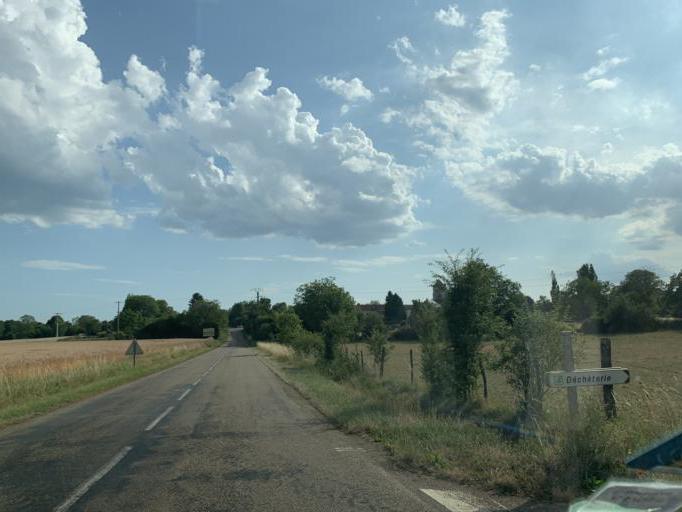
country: FR
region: Bourgogne
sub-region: Departement de l'Yonne
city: Fontenailles
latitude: 47.5058
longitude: 3.3513
